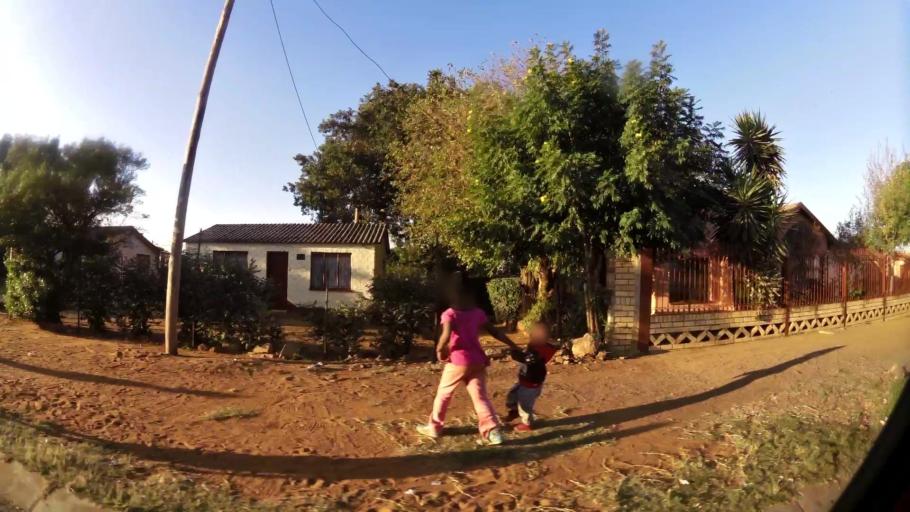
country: ZA
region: North-West
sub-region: Bojanala Platinum District Municipality
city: Rustenburg
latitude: -25.6370
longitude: 27.2090
